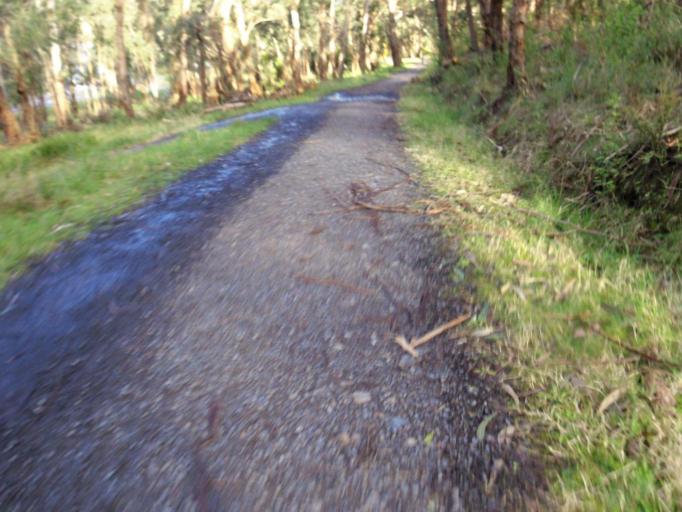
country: AU
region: Victoria
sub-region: Yarra Ranges
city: Ferny Creek
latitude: -37.8909
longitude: 145.3162
